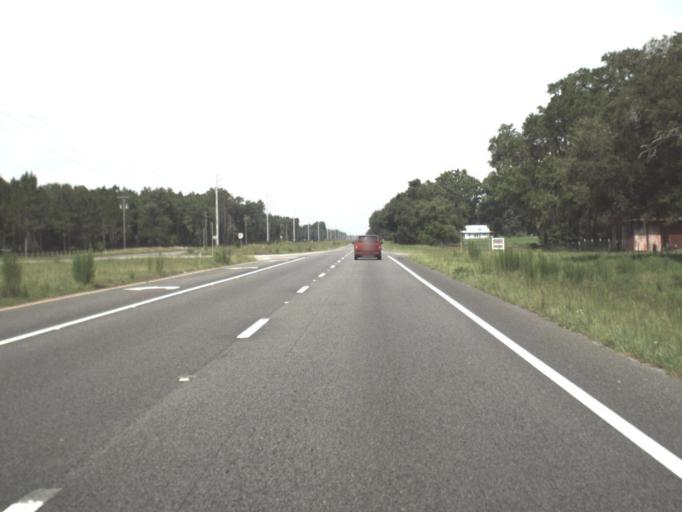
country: US
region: Florida
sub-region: Levy County
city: Chiefland
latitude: 29.4751
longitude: -82.7883
